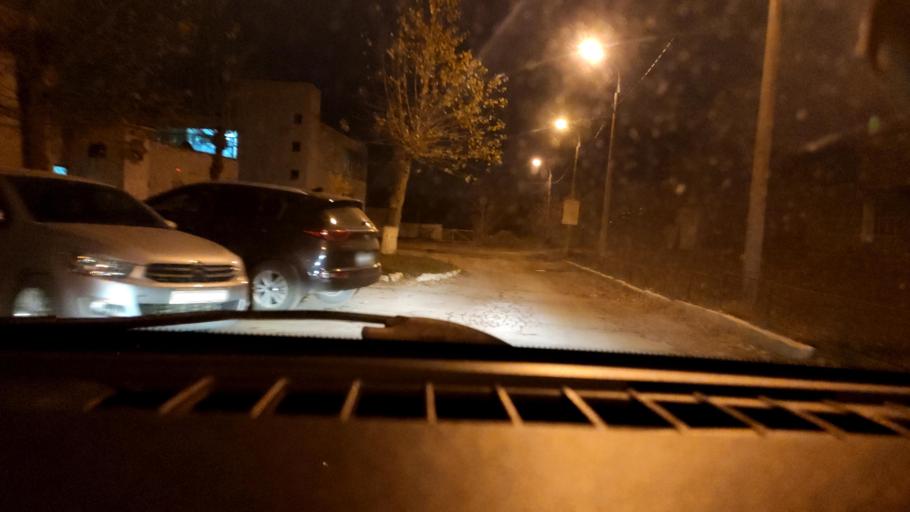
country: RU
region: Samara
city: Samara
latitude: 53.2419
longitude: 50.2511
